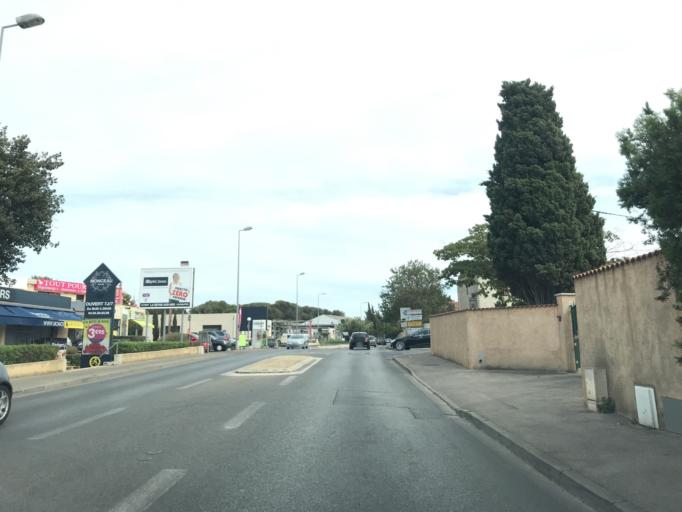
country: FR
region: Provence-Alpes-Cote d'Azur
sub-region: Departement du Var
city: Six-Fours-les-Plages
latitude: 43.0879
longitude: 5.8540
